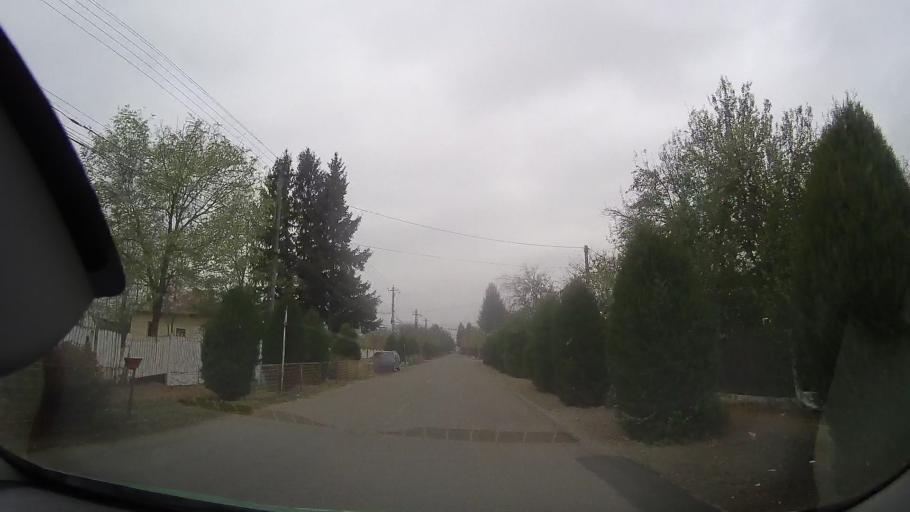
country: RO
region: Buzau
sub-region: Comuna Bradeanu
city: Bradeanu
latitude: 44.9235
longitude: 26.8653
